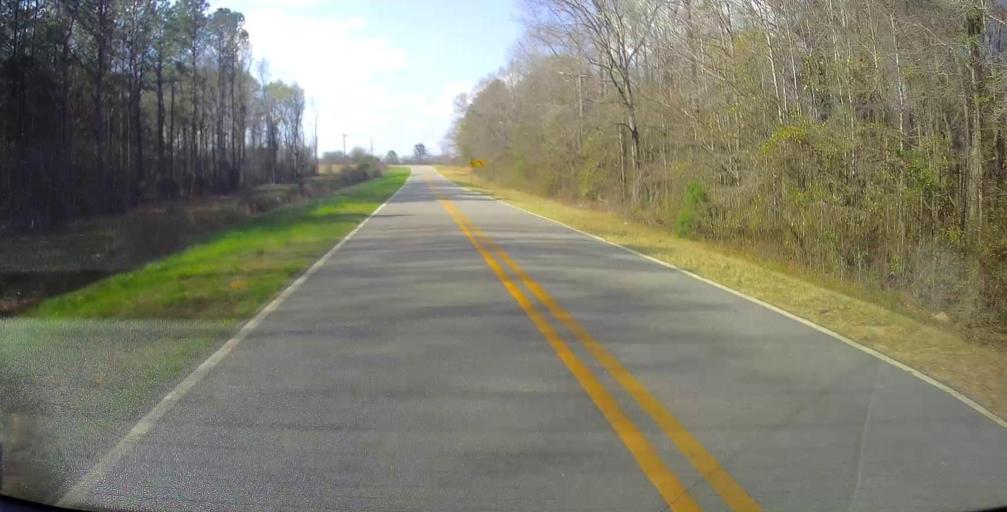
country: US
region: Georgia
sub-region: Wilkinson County
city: Irwinton
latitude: 32.6241
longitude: -83.0915
